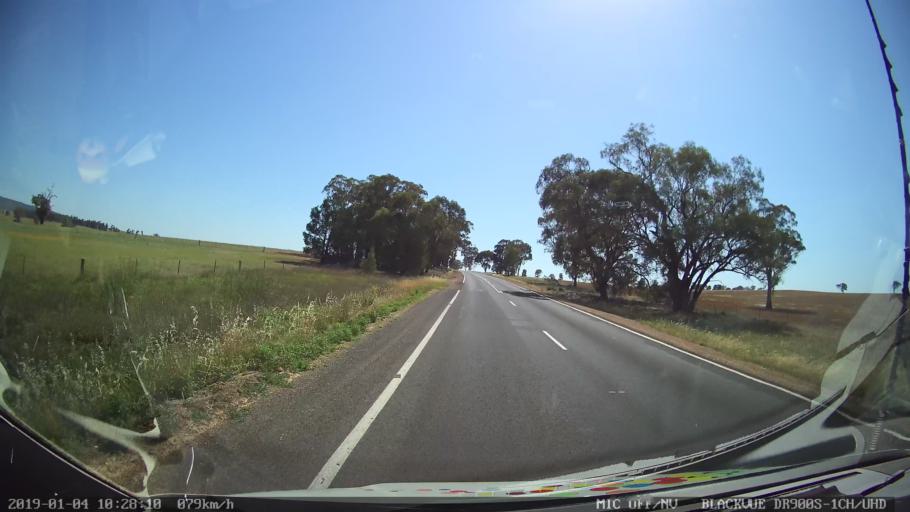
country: AU
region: New South Wales
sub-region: Cabonne
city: Canowindra
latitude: -33.3649
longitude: 148.6064
